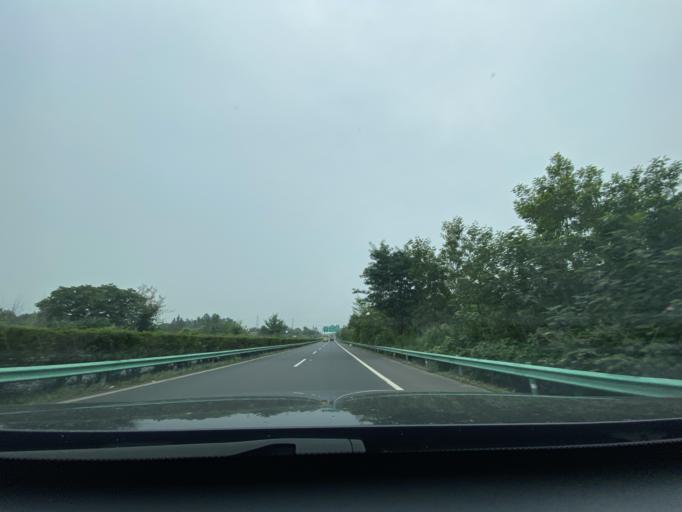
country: CN
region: Sichuan
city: Longquan
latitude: 30.3270
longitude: 104.1205
